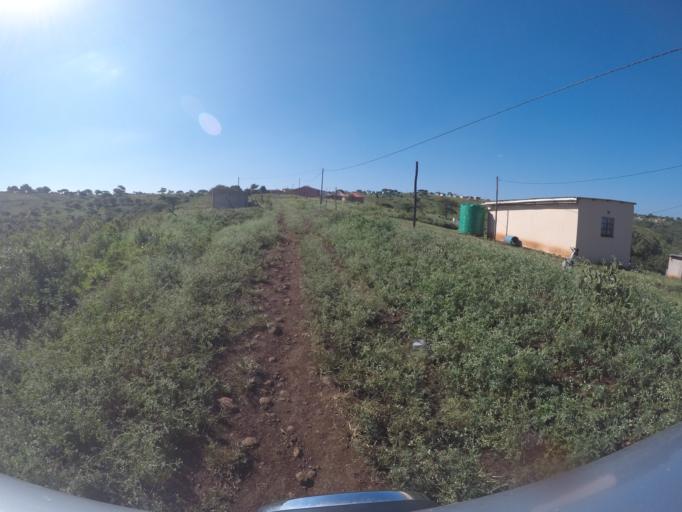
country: ZA
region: KwaZulu-Natal
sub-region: uThungulu District Municipality
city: Empangeni
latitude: -28.5751
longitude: 31.7321
